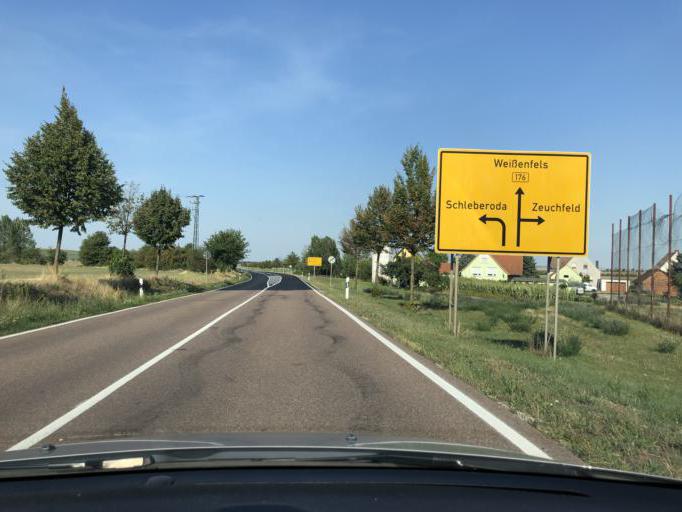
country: DE
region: Saxony-Anhalt
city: Goseck
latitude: 51.2382
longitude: 11.8264
